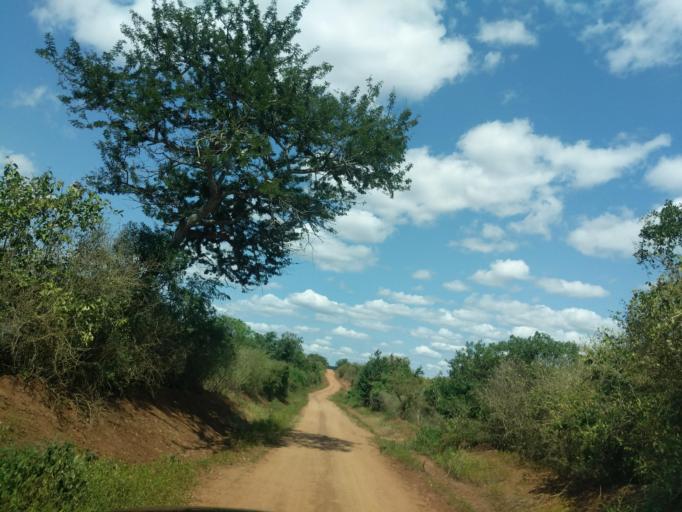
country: TZ
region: Tanga
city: Chanika
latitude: -5.5098
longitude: 38.3655
